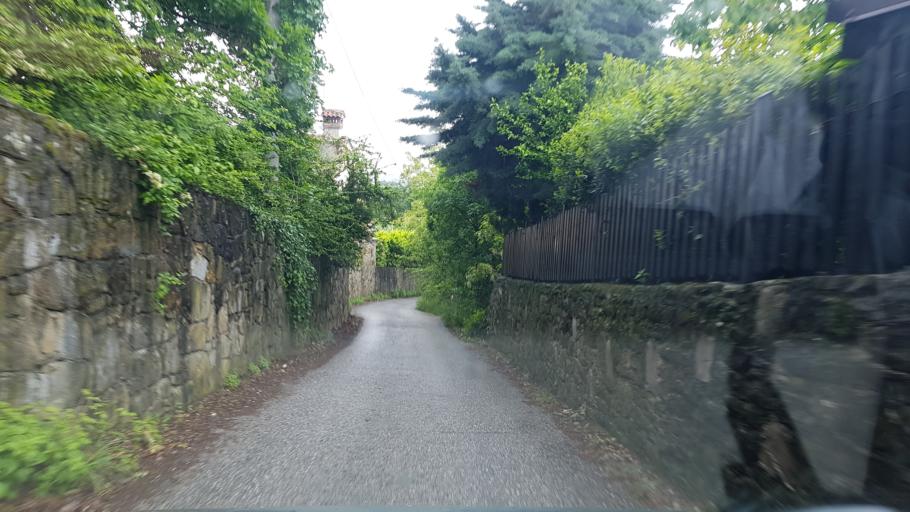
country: IT
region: Friuli Venezia Giulia
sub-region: Provincia di Trieste
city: Villa Opicina
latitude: 45.6740
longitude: 13.7855
